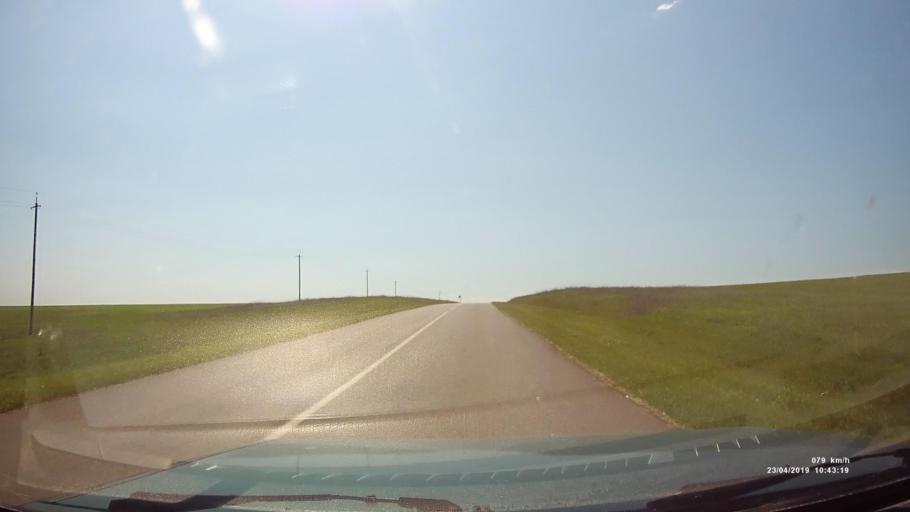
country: RU
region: Kalmykiya
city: Yashalta
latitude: 46.4718
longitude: 42.6493
